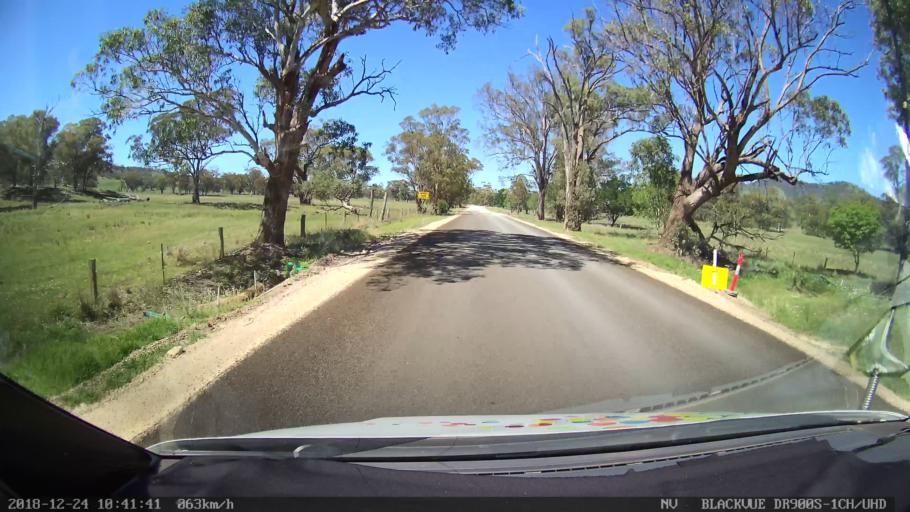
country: AU
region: New South Wales
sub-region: Upper Hunter Shire
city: Merriwa
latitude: -31.8710
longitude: 150.4575
